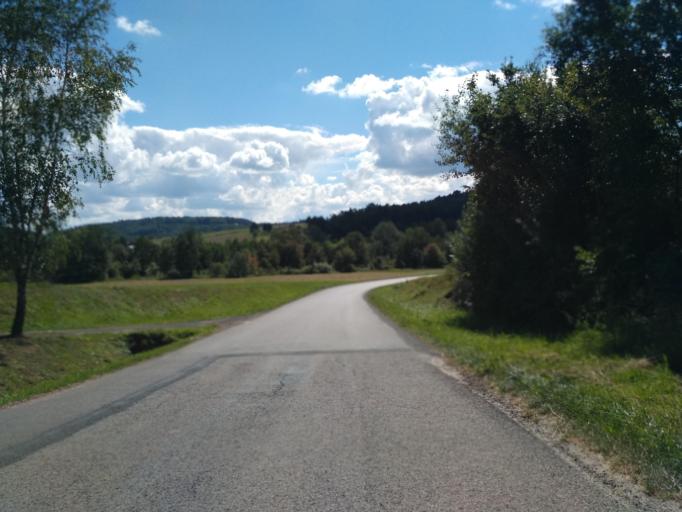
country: PL
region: Subcarpathian Voivodeship
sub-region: Powiat jasielski
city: Skolyszyn
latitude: 49.8003
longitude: 21.3148
